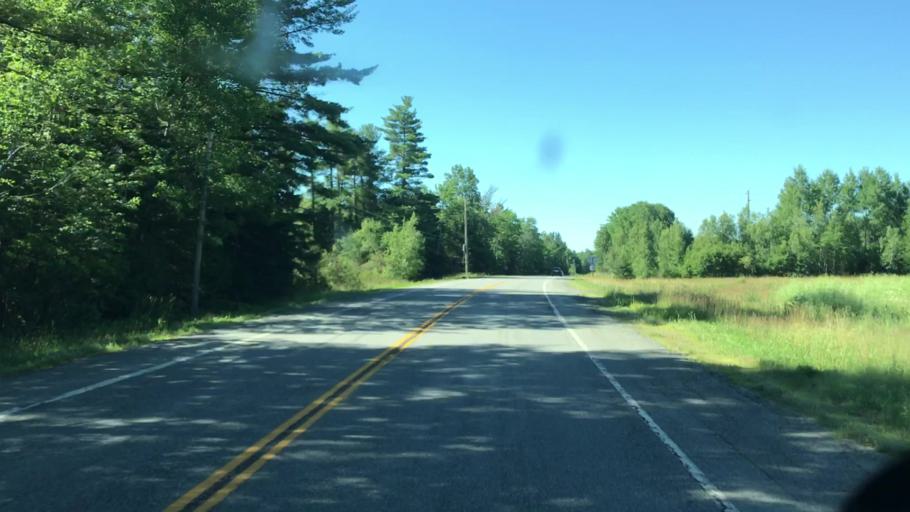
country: US
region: Maine
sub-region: Penobscot County
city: Howland
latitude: 45.2520
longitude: -68.6378
